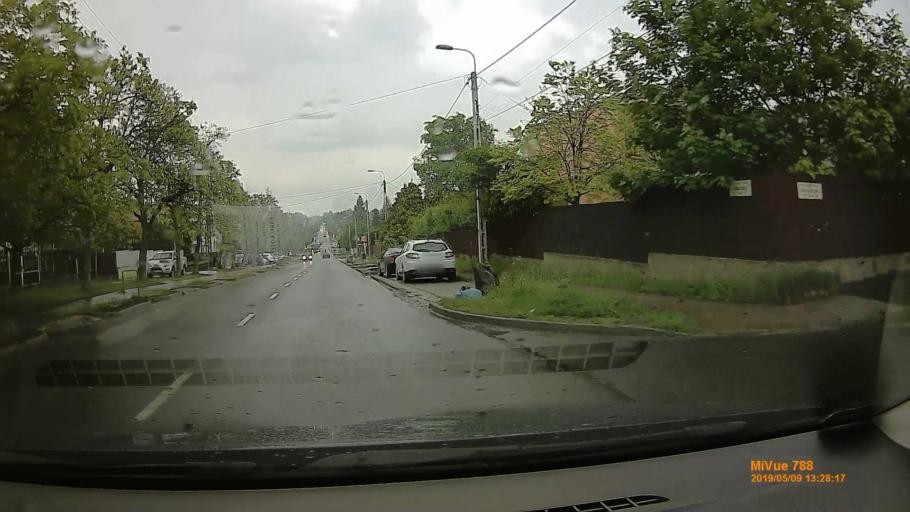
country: HU
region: Budapest
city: Budapest XVI. keruelet
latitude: 47.5345
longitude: 19.1956
